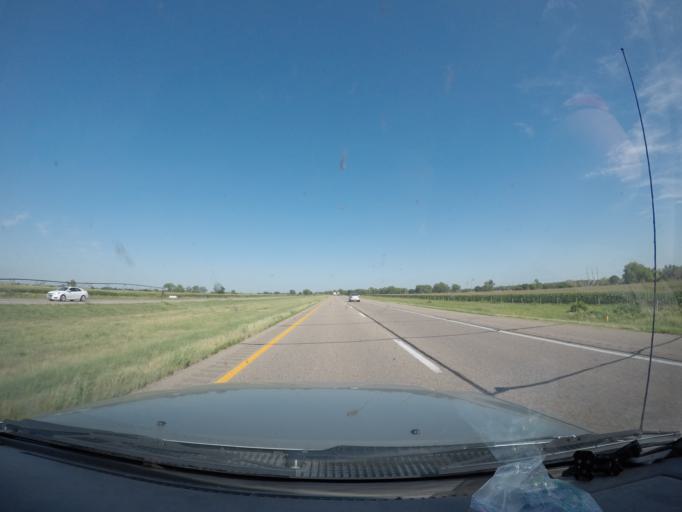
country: US
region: Nebraska
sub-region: Buffalo County
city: Kearney
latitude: 40.6875
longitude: -99.3280
